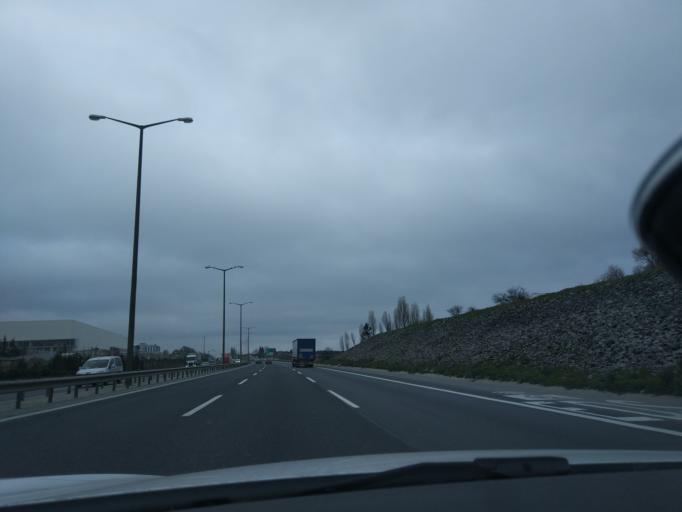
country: TR
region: Istanbul
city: Esenyurt
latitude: 41.0731
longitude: 28.6478
